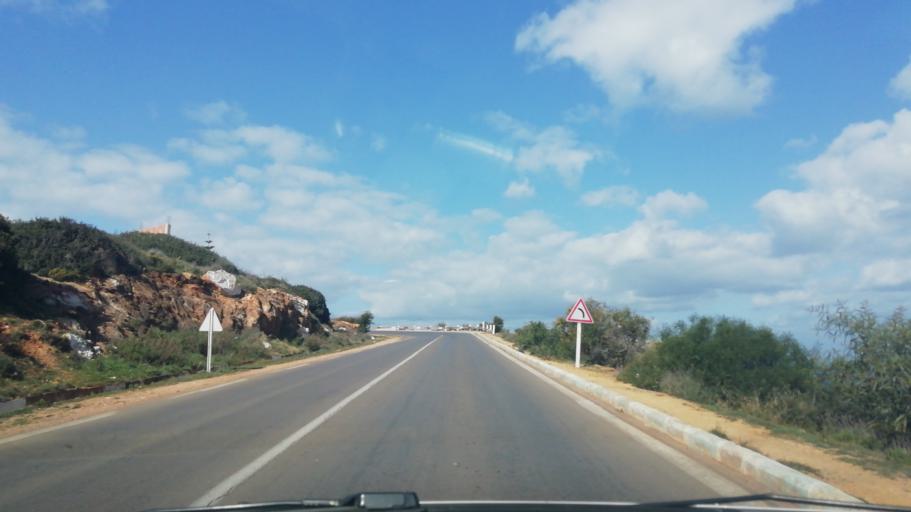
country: DZ
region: Relizane
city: Mazouna
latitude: 36.3285
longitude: 0.6899
